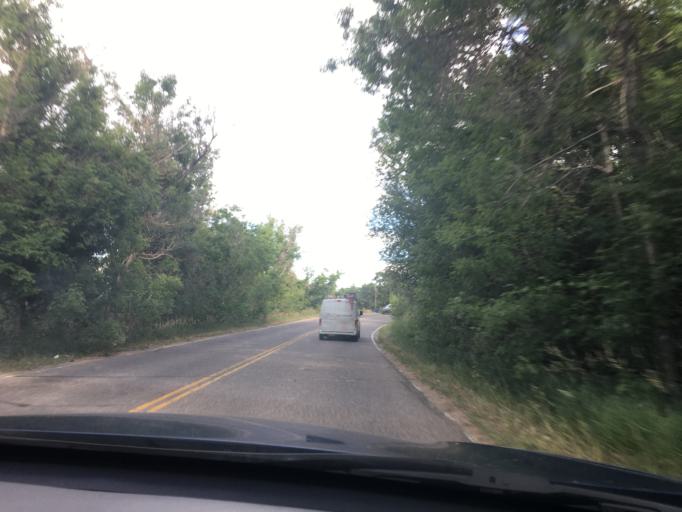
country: US
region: Colorado
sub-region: Jefferson County
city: Applewood
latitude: 39.7659
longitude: -105.1835
